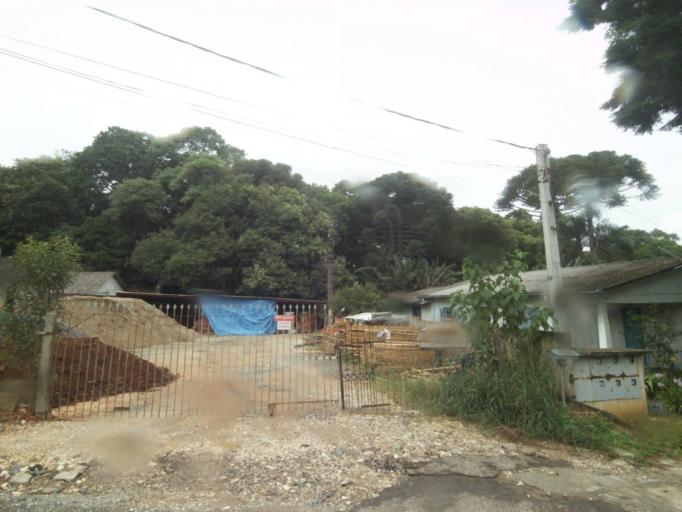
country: BR
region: Parana
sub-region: Curitiba
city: Curitiba
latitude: -25.4477
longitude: -49.3479
